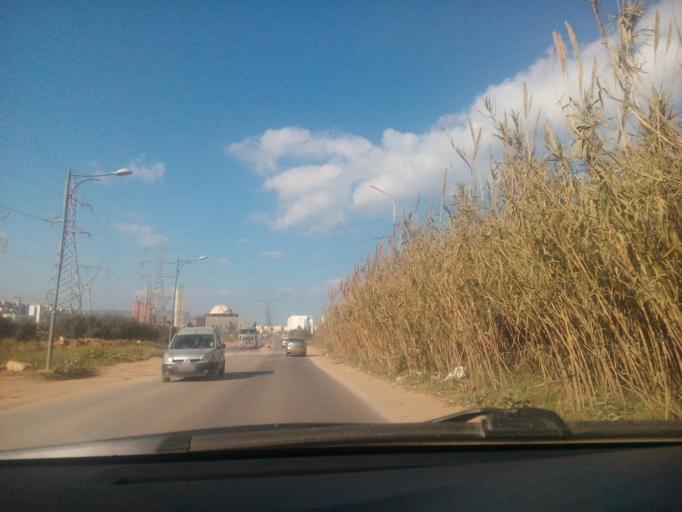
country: DZ
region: Oran
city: Es Senia
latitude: 35.6765
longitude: -0.5960
